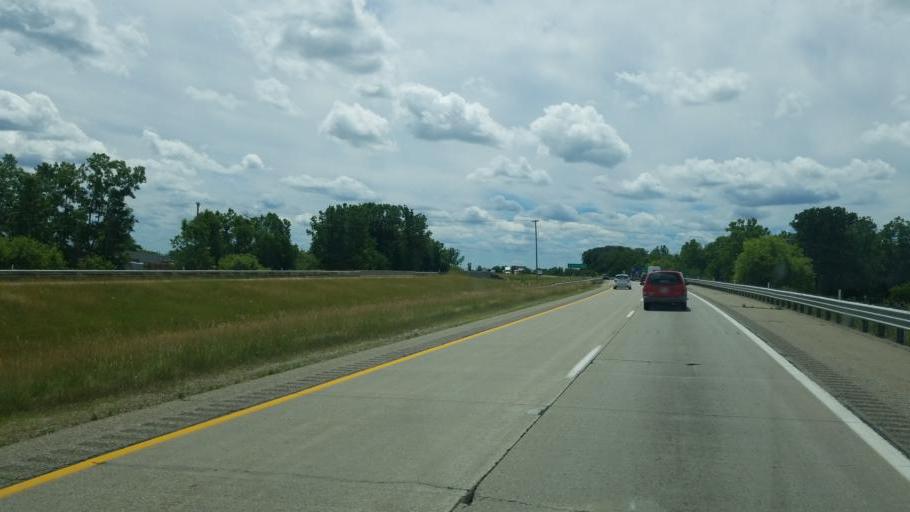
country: US
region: Michigan
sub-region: Eaton County
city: Charlotte
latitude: 42.5833
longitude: -84.8160
